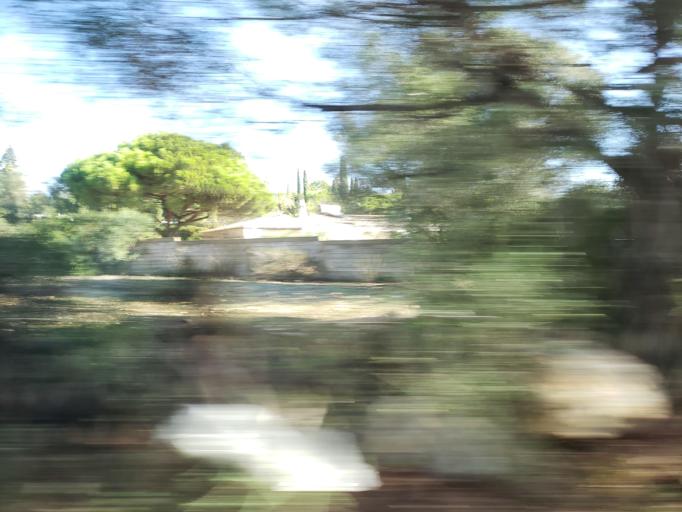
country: PT
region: Faro
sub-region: Portimao
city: Alvor
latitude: 37.1835
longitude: -8.5850
